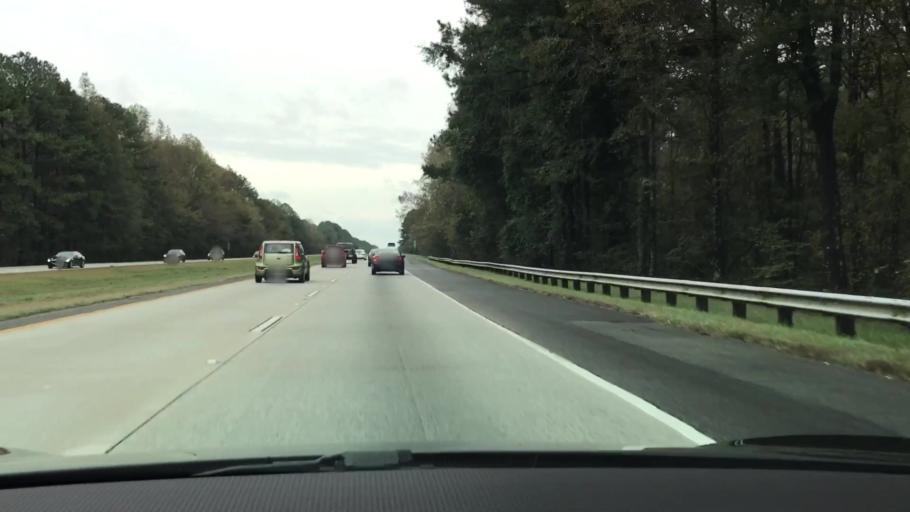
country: US
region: Georgia
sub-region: Greene County
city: Union Point
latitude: 33.5465
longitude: -83.0332
